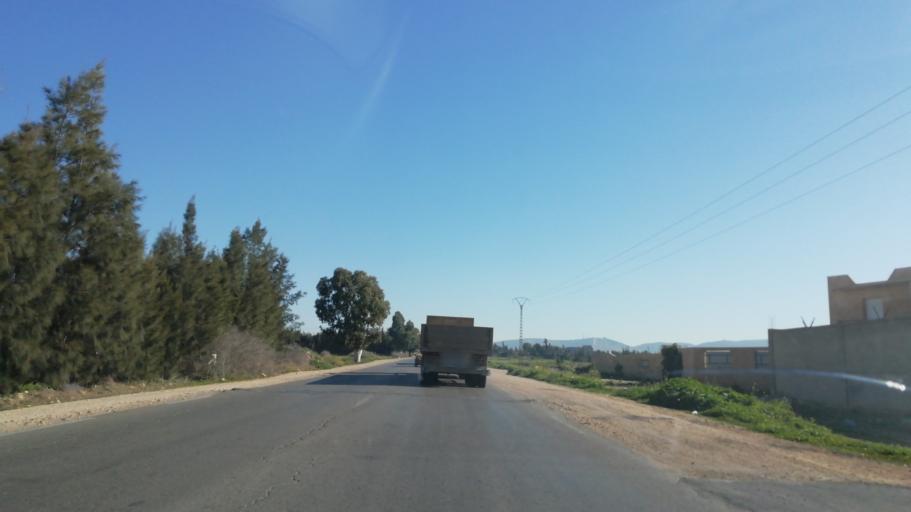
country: DZ
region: Relizane
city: Zemoura
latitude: 35.7460
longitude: 0.6970
